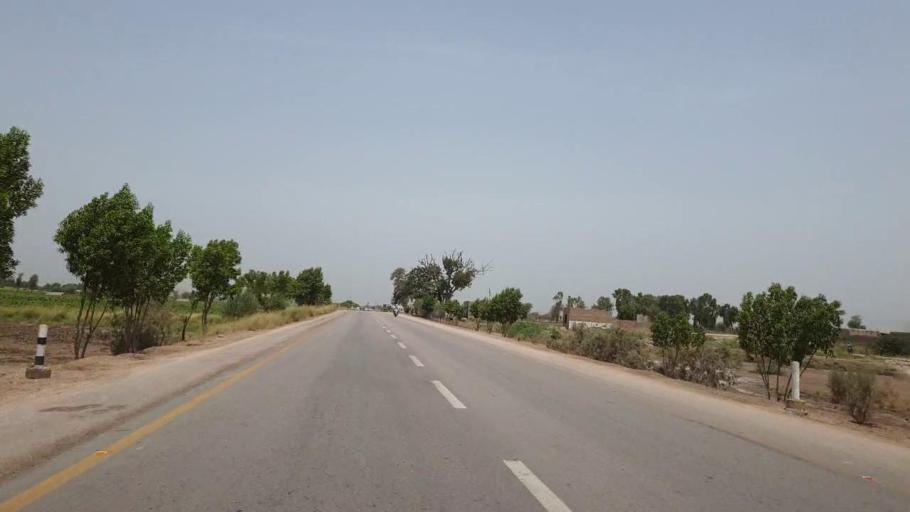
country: PK
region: Sindh
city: Nawabshah
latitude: 26.2265
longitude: 68.4914
